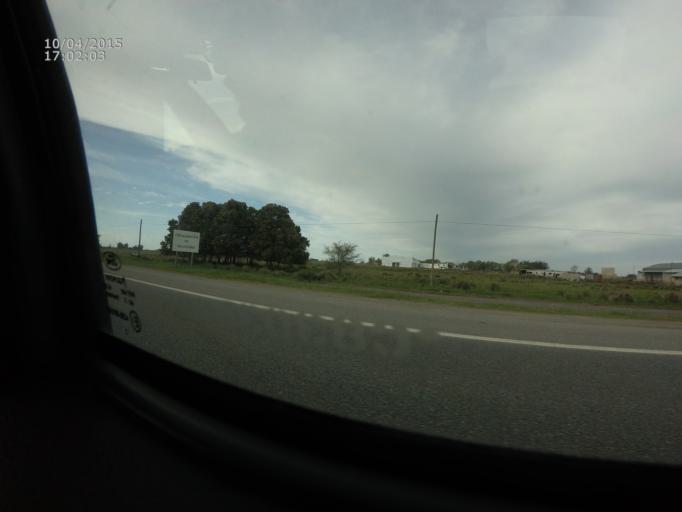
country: AR
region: Buenos Aires
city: Coronel Vidal
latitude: -37.4388
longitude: -57.7256
